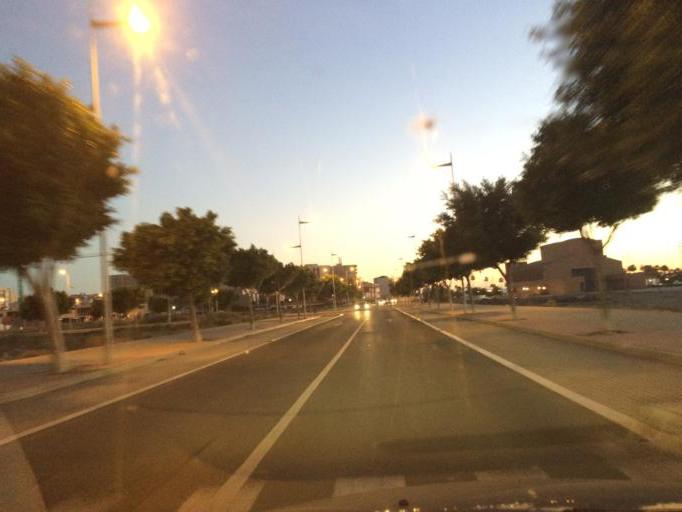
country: ES
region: Andalusia
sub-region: Provincia de Almeria
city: Almeria
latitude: 36.8271
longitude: -2.4431
